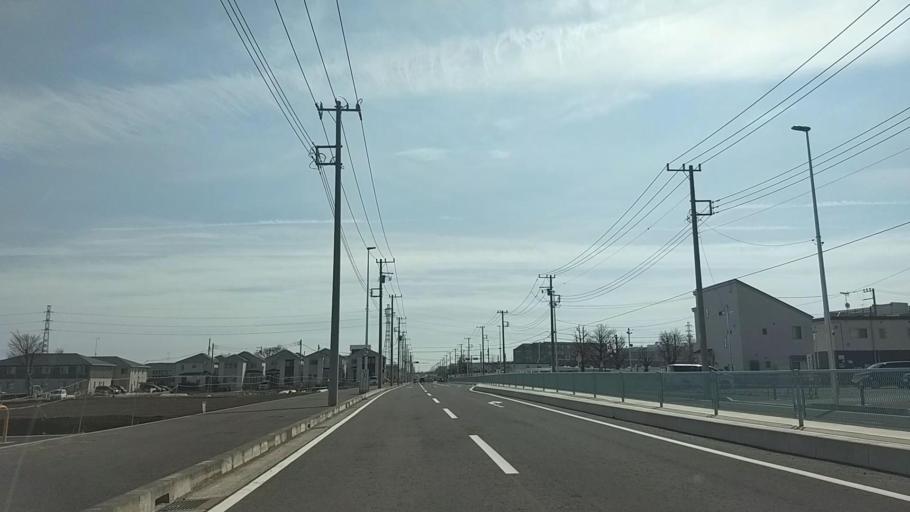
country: JP
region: Kanagawa
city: Fujisawa
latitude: 35.4042
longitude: 139.4547
